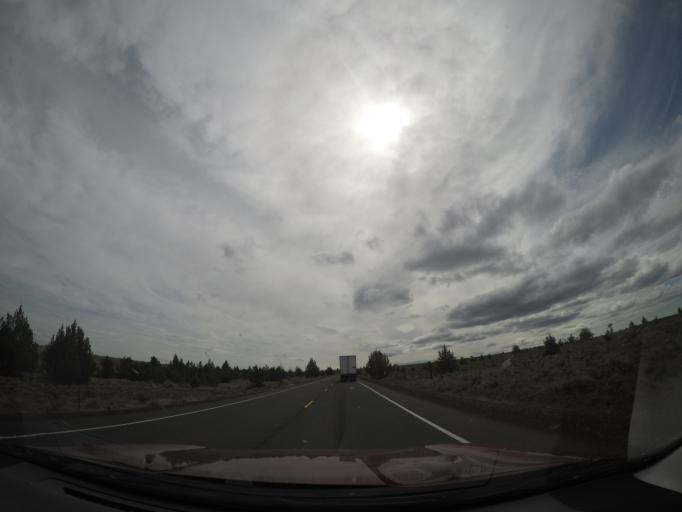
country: US
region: Oregon
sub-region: Sherman County
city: Moro
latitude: 45.0358
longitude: -120.7246
